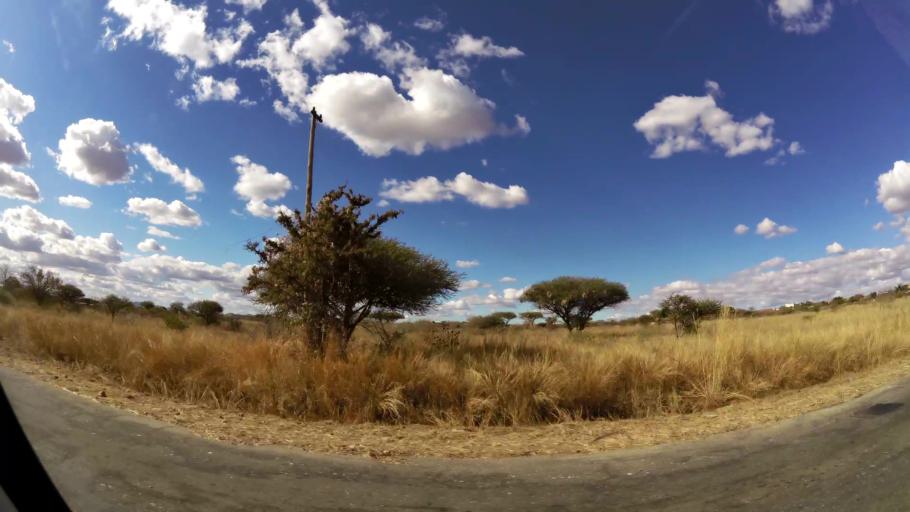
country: ZA
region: Limpopo
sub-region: Capricorn District Municipality
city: Polokwane
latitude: -23.8778
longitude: 29.4807
